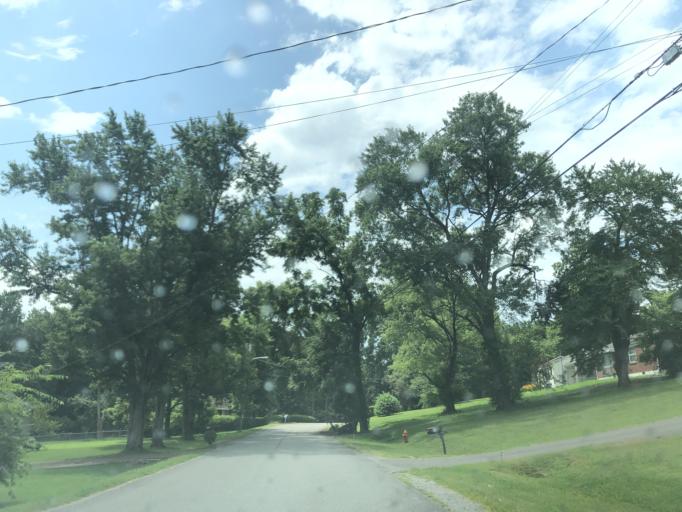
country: US
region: Tennessee
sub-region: Davidson County
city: Lakewood
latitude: 36.1607
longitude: -86.6520
